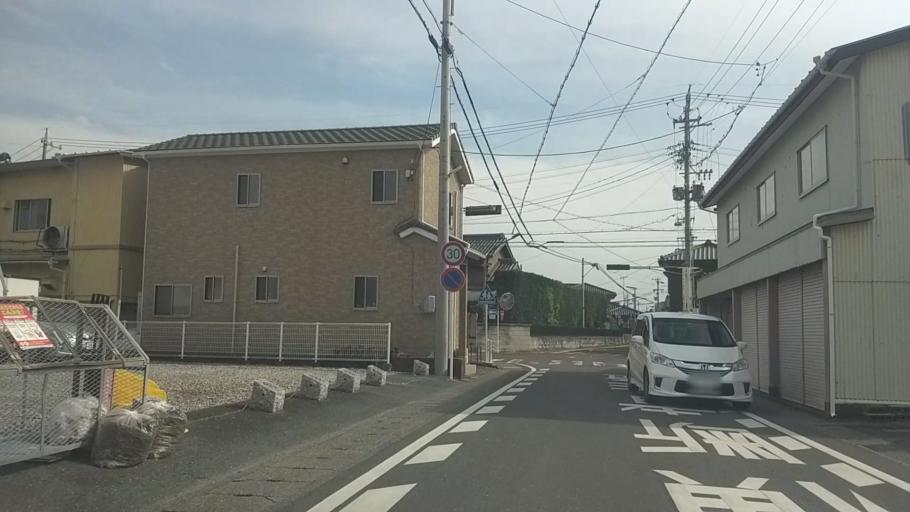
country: JP
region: Shizuoka
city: Kosai-shi
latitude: 34.7024
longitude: 137.6293
